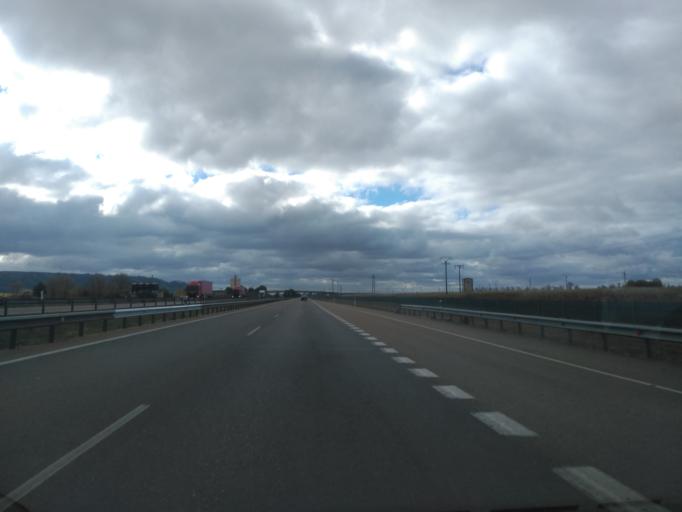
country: ES
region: Castille and Leon
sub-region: Provincia de Valladolid
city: Cabezon
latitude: 41.7733
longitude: -4.6205
